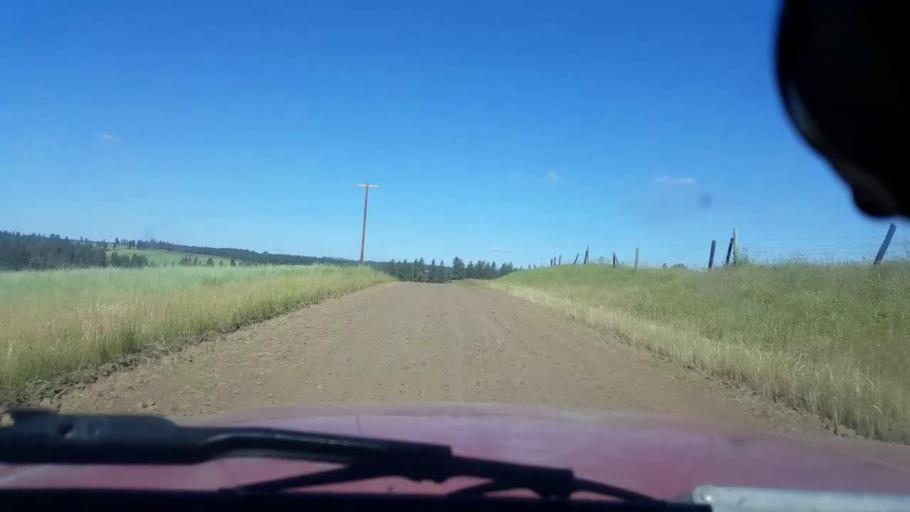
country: US
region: Washington
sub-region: Garfield County
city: Pomeroy
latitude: 45.9845
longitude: -117.4651
